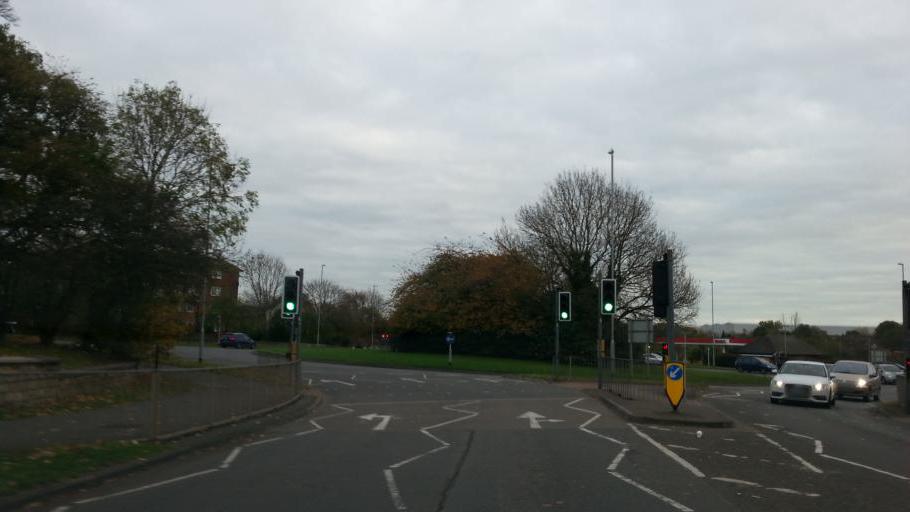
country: GB
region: England
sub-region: Northamptonshire
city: Corby
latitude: 52.4852
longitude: -0.6990
